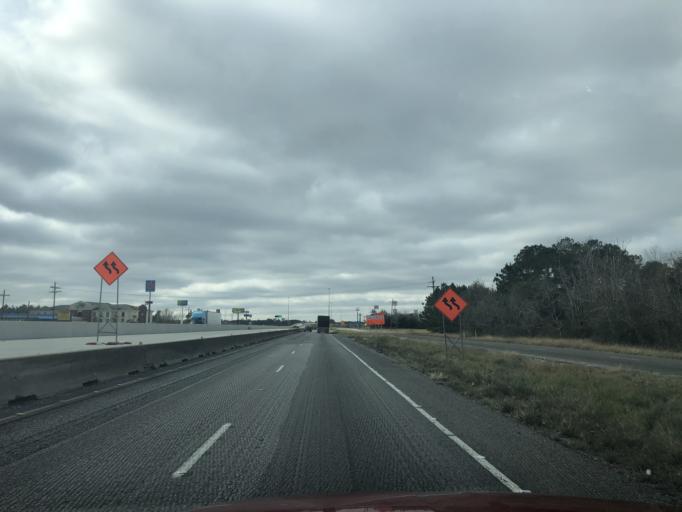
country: US
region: Texas
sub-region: Chambers County
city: Winnie
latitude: 29.8394
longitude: -94.3790
